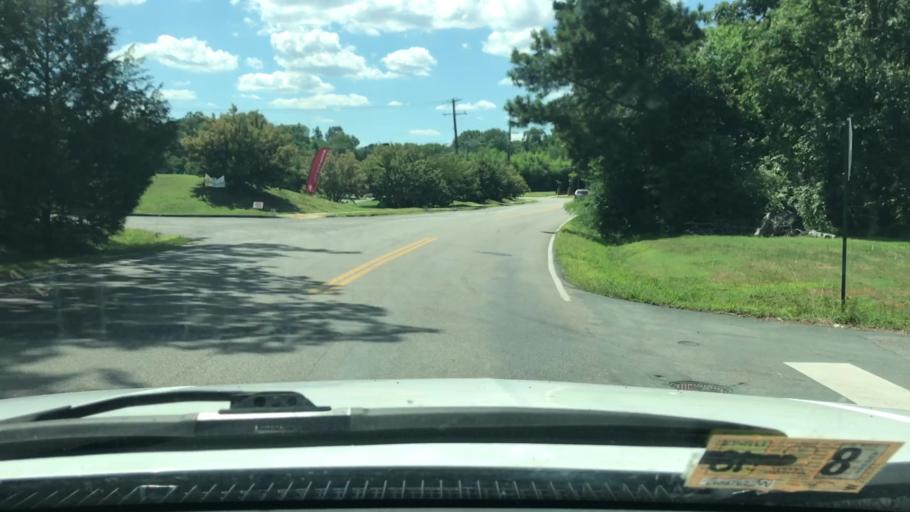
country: US
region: Virginia
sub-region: Henrico County
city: East Highland Park
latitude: 37.5730
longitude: -77.4065
